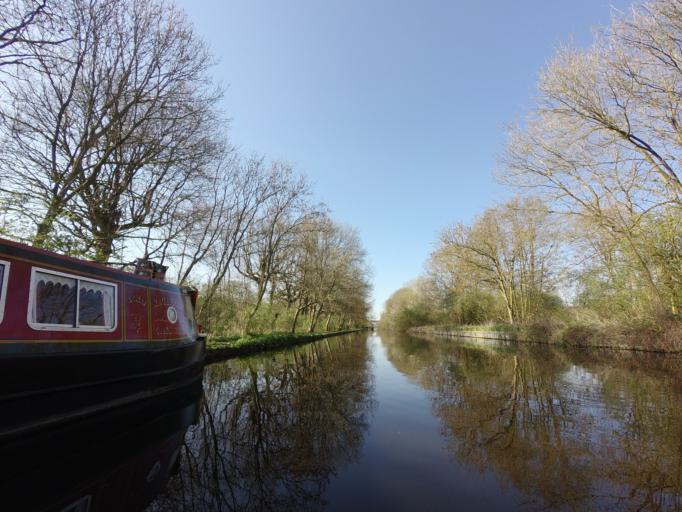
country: GB
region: England
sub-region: Buckinghamshire
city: Denham
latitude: 51.5732
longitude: -0.4821
